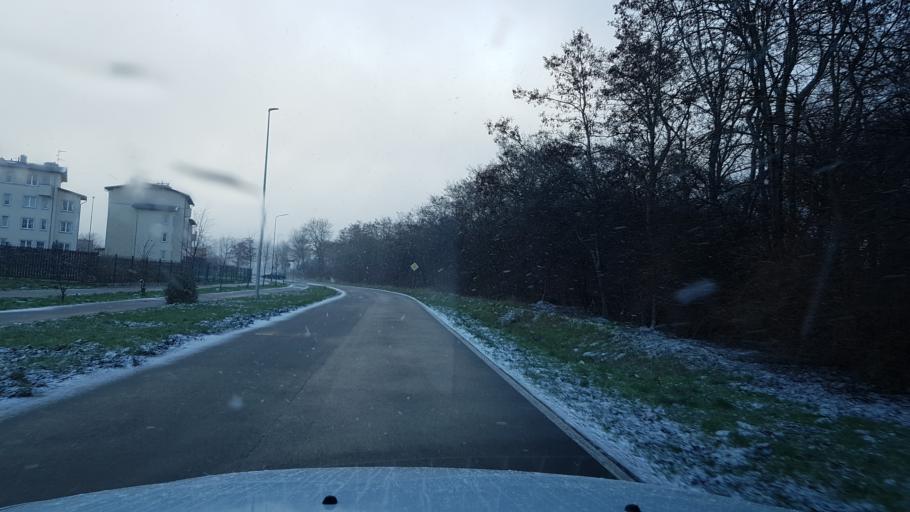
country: PL
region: West Pomeranian Voivodeship
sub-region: Powiat gryficki
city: Trzebiatow
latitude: 54.0567
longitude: 15.2878
